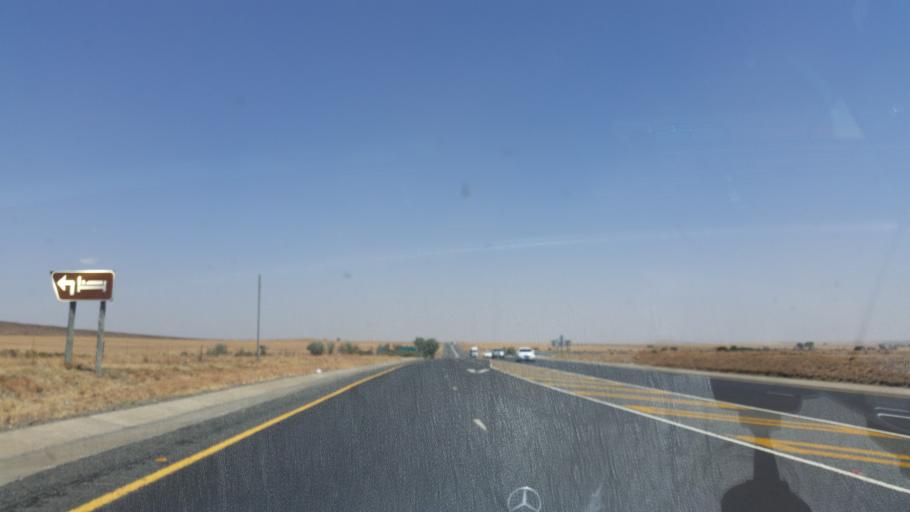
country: ZA
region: Orange Free State
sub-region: Lejweleputswa District Municipality
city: Brandfort
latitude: -28.8147
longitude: 26.6694
